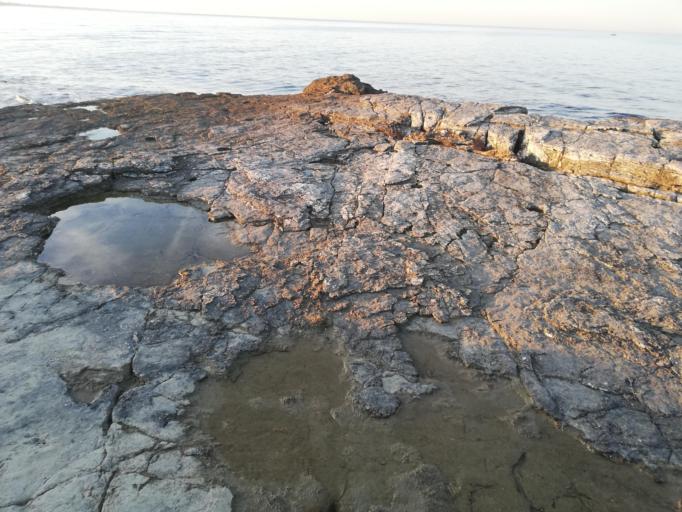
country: IT
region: Apulia
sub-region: Provincia di Bari
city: Giovinazzo
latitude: 41.1859
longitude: 16.6551
